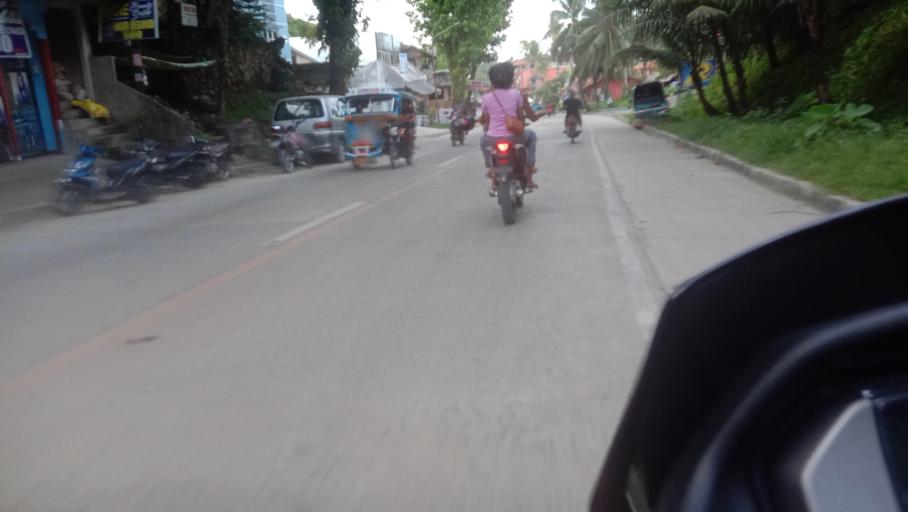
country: PH
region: Caraga
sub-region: Province of Surigao del Sur
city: Barobo
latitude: 8.5295
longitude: 126.1196
